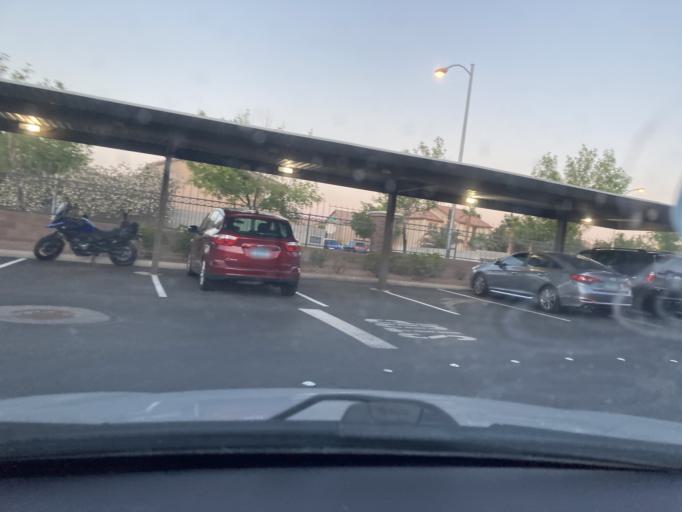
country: US
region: Nevada
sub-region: Clark County
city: Enterprise
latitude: 36.0569
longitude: -115.2885
